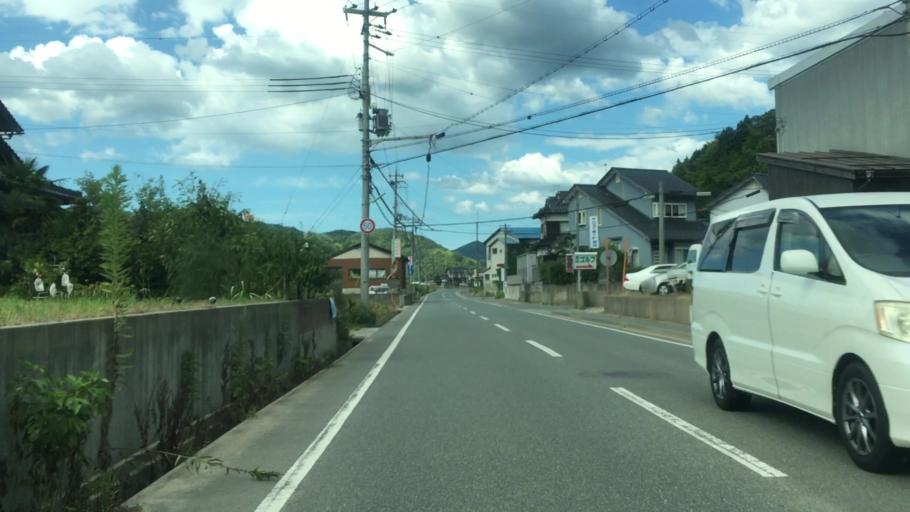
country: JP
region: Hyogo
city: Toyooka
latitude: 35.5530
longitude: 134.7929
